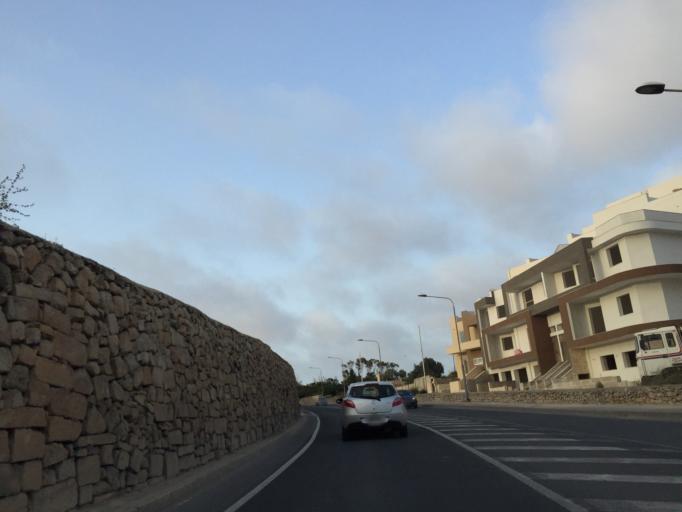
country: MT
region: Il-Mosta
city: Mosta
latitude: 35.9110
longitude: 14.4132
